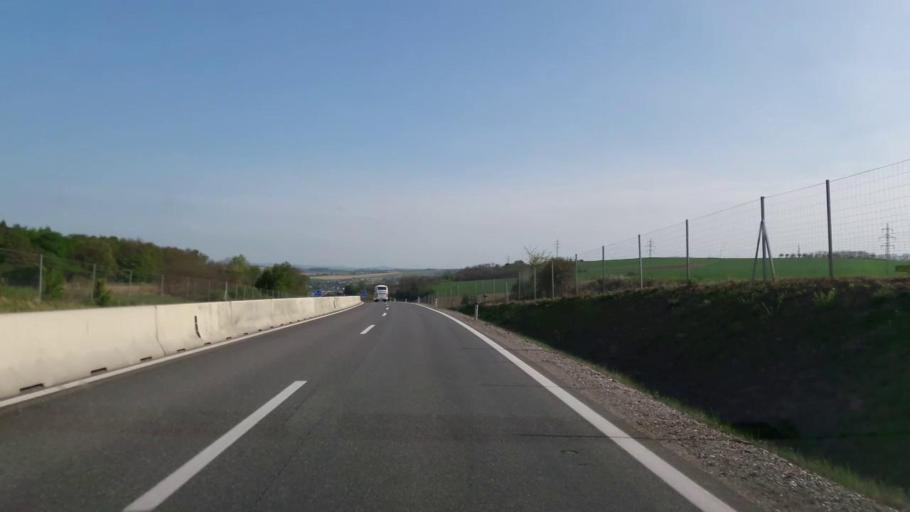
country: AT
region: Lower Austria
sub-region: Politischer Bezirk Hollabrunn
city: Hollabrunn
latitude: 48.5292
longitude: 16.0816
